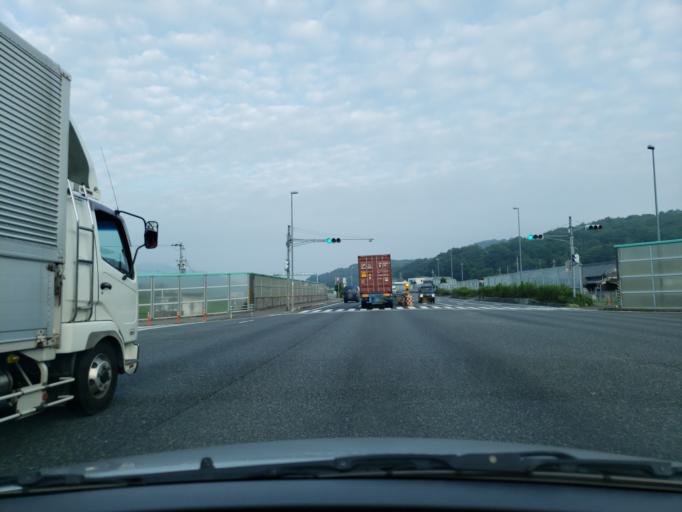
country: JP
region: Hyogo
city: Aioi
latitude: 34.8259
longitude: 134.4543
